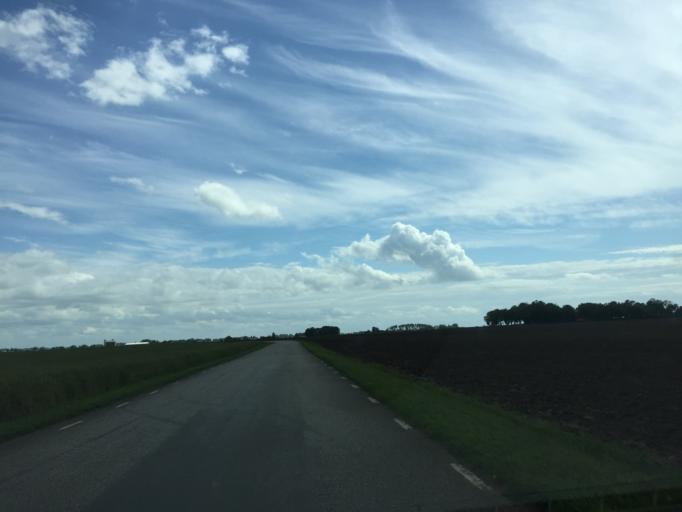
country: SE
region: OEstergoetland
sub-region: Vadstena Kommun
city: Vadstena
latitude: 58.4493
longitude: 14.8384
